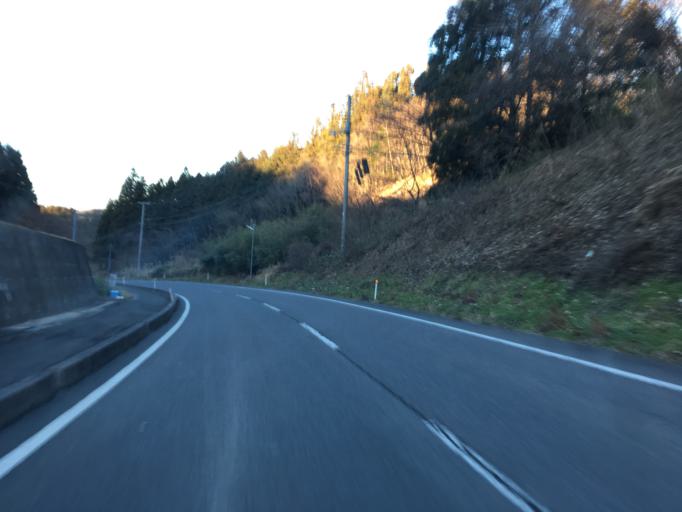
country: JP
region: Fukushima
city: Ishikawa
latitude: 37.2059
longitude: 140.5652
